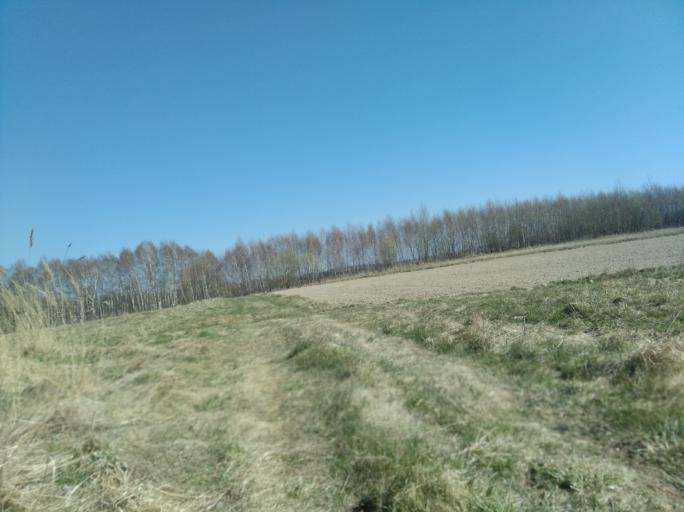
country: PL
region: Subcarpathian Voivodeship
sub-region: Powiat strzyzowski
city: Jawornik
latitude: 49.8523
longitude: 21.8547
